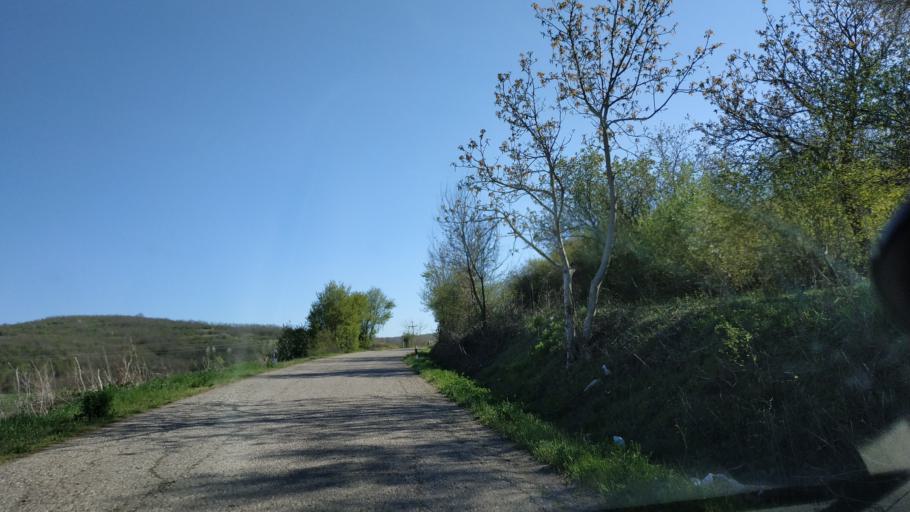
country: RS
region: Central Serbia
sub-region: Nisavski Okrug
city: Aleksinac
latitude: 43.4979
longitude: 21.6749
